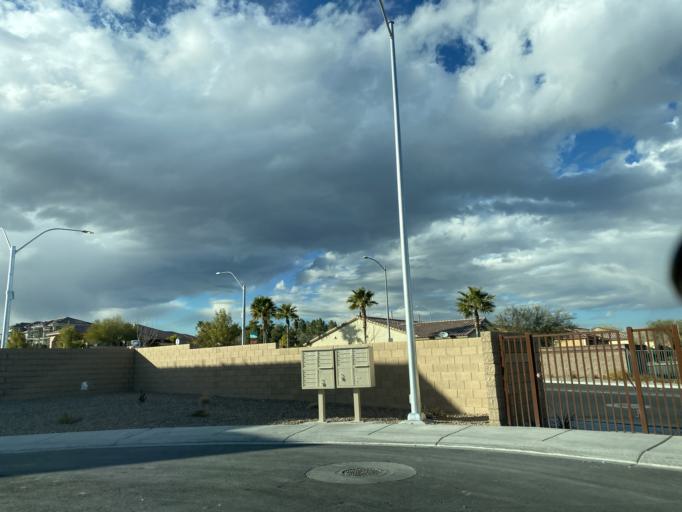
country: US
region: Nevada
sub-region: Clark County
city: Summerlin South
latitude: 36.2844
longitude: -115.3052
